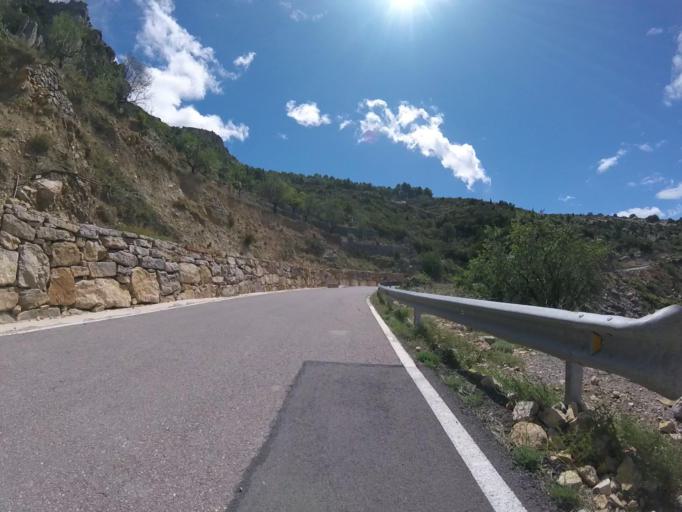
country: ES
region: Valencia
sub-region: Provincia de Castello
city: Sierra-Engarceran
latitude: 40.2826
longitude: -0.0317
